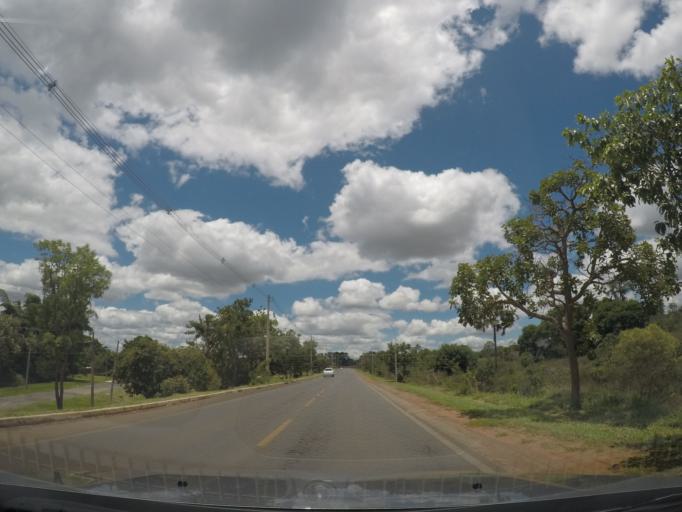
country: BR
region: Federal District
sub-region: Brasilia
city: Brasilia
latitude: -15.7783
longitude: -47.8097
